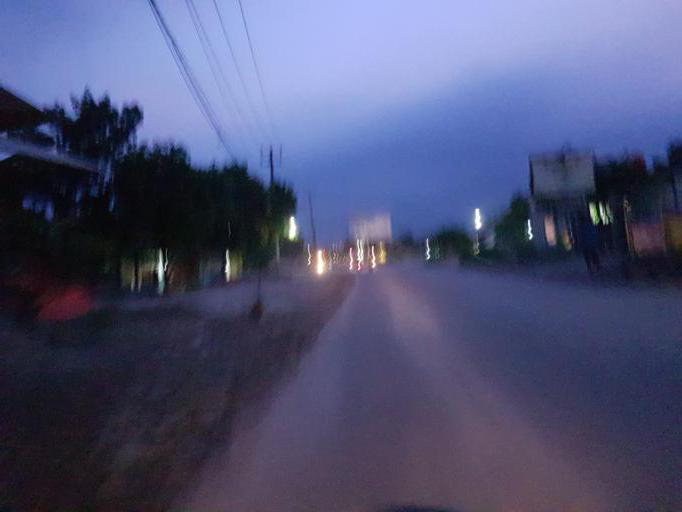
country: ID
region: West Java
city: Serpong
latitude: -6.3129
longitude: 106.6555
